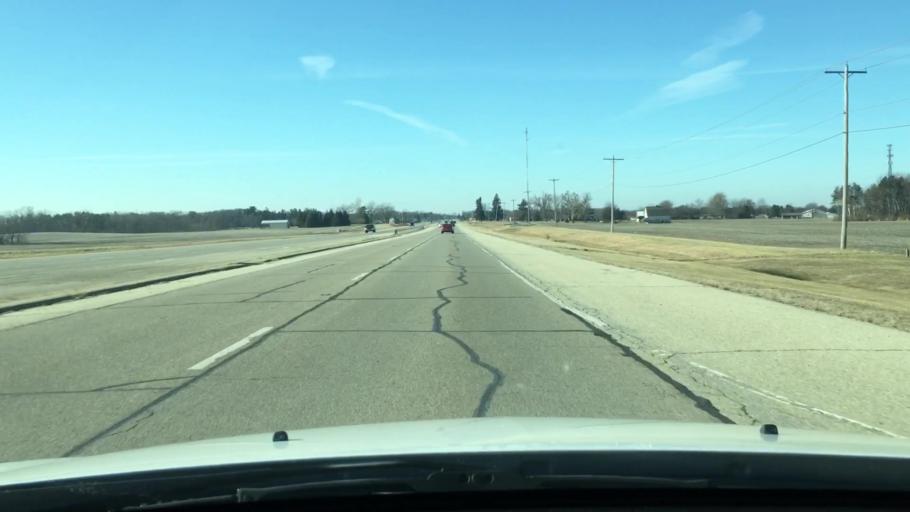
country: US
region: Illinois
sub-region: Woodford County
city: Germantown Hills
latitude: 40.7739
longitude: -89.4328
